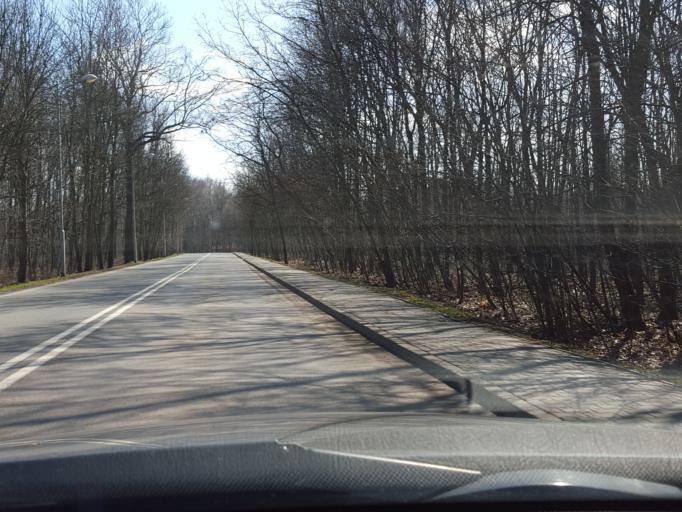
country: PL
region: Silesian Voivodeship
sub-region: Ruda Slaska
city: Ruda Slaska
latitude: 50.2363
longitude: 18.8559
